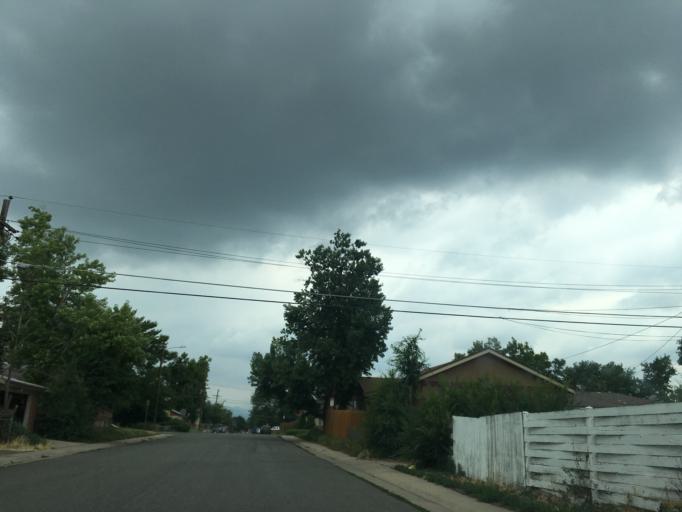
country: US
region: Colorado
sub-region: Arapahoe County
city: Sheridan
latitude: 39.6842
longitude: -105.0172
